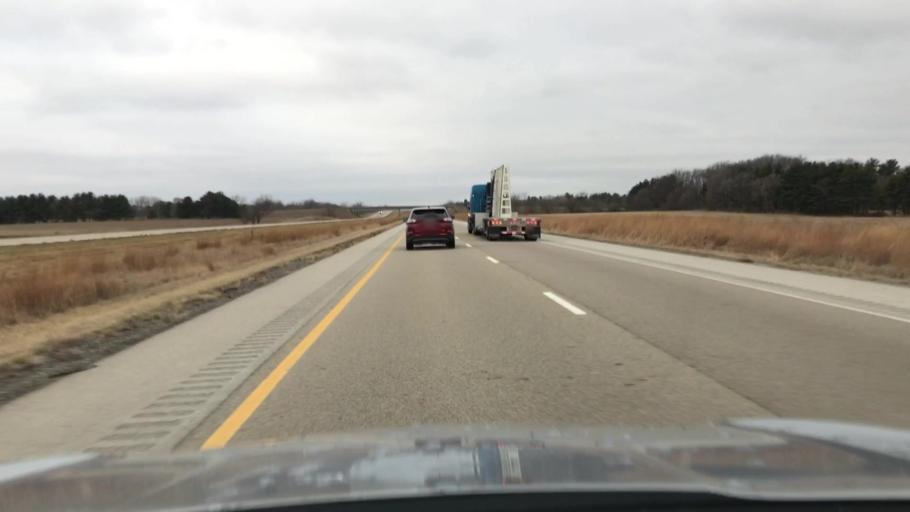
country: US
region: Illinois
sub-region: Logan County
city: Lincoln
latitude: 40.1819
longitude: -89.3516
